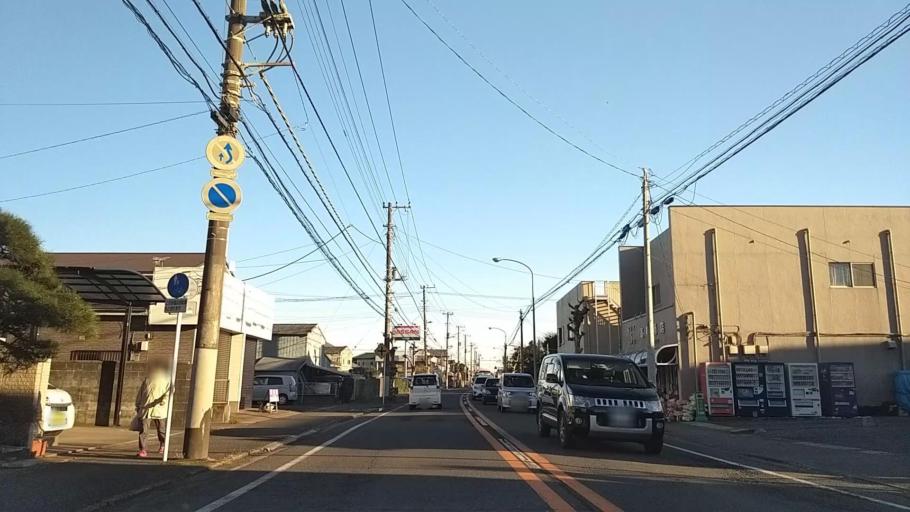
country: JP
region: Chiba
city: Hasaki
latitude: 35.7384
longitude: 140.8017
